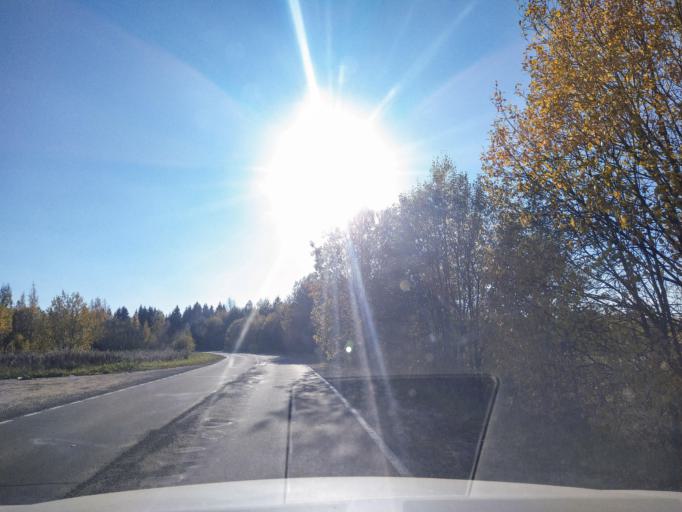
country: RU
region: Leningrad
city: Siverskiy
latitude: 59.3111
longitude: 30.0305
